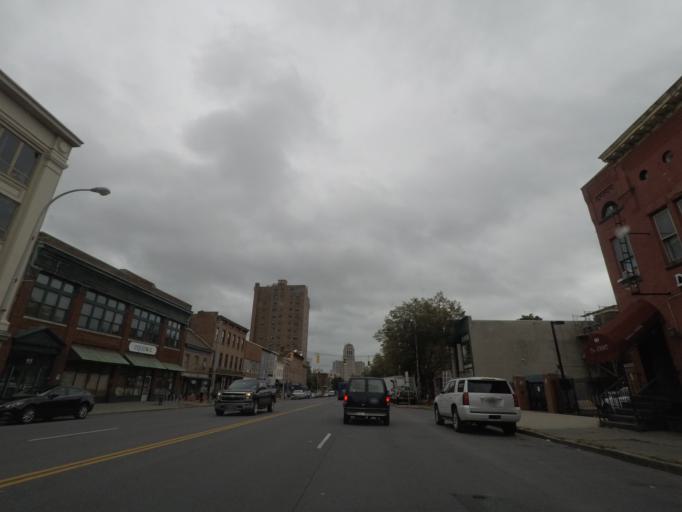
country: US
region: New York
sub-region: Albany County
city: Albany
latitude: 42.6596
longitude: -73.7666
